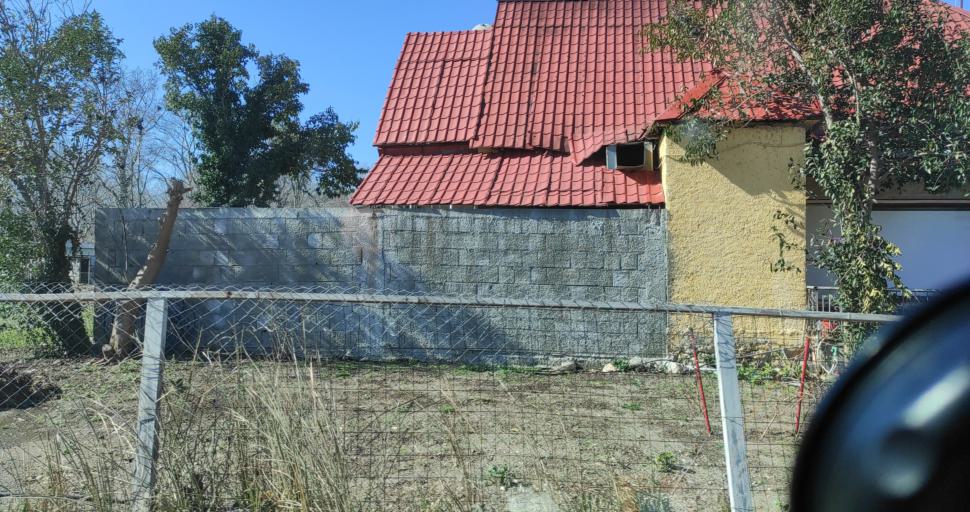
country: AL
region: Shkoder
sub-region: Rrethi i Shkodres
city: Velipoje
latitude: 41.8671
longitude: 19.4060
